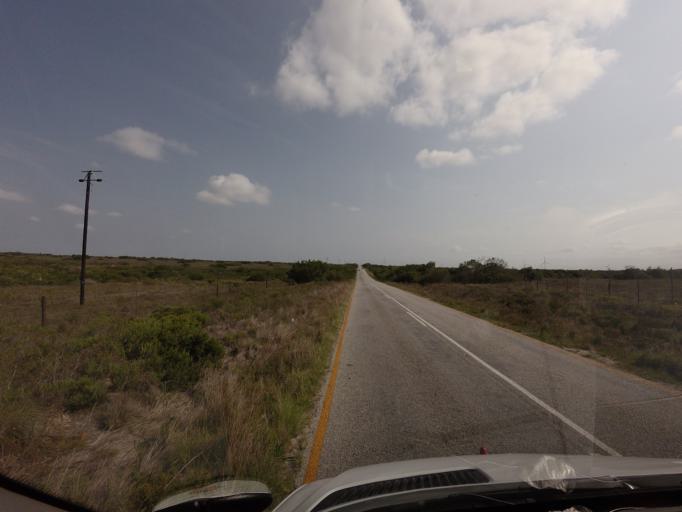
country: ZA
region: Eastern Cape
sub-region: Nelson Mandela Bay Metropolitan Municipality
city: Uitenhage
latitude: -33.7013
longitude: 25.5888
